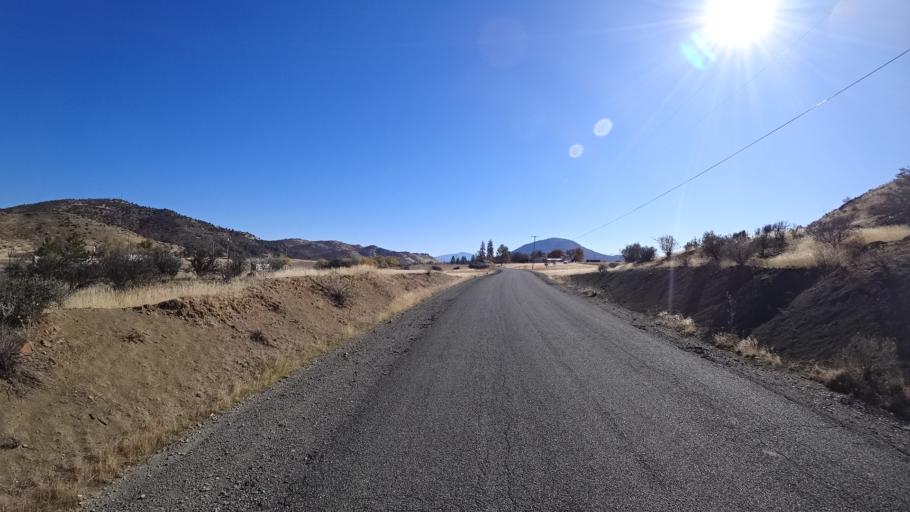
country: US
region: California
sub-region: Siskiyou County
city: Yreka
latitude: 41.9260
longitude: -122.5816
